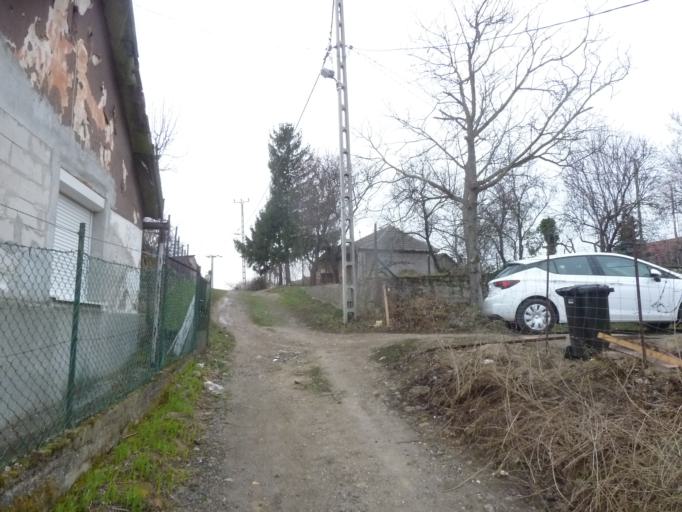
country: HU
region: Fejer
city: Racalmas
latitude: 47.0214
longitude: 18.9441
